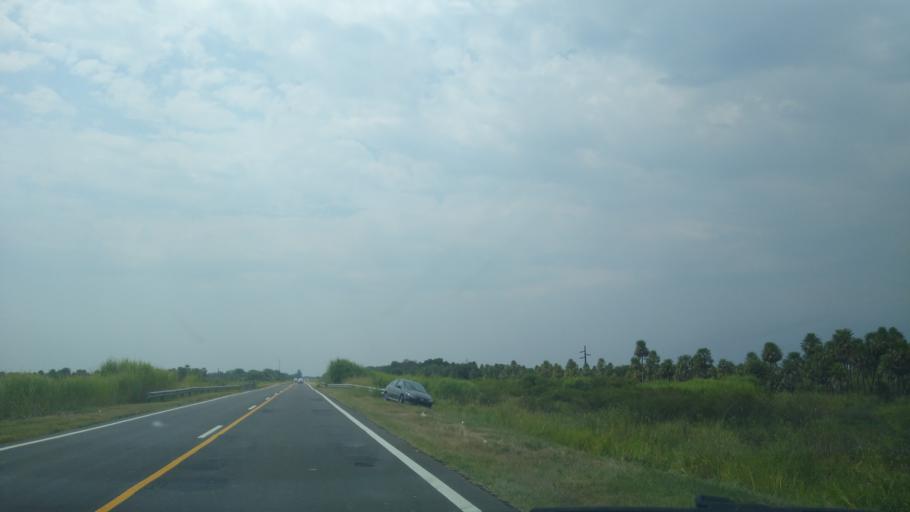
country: AR
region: Chaco
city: Margarita Belen
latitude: -27.1105
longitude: -58.9675
